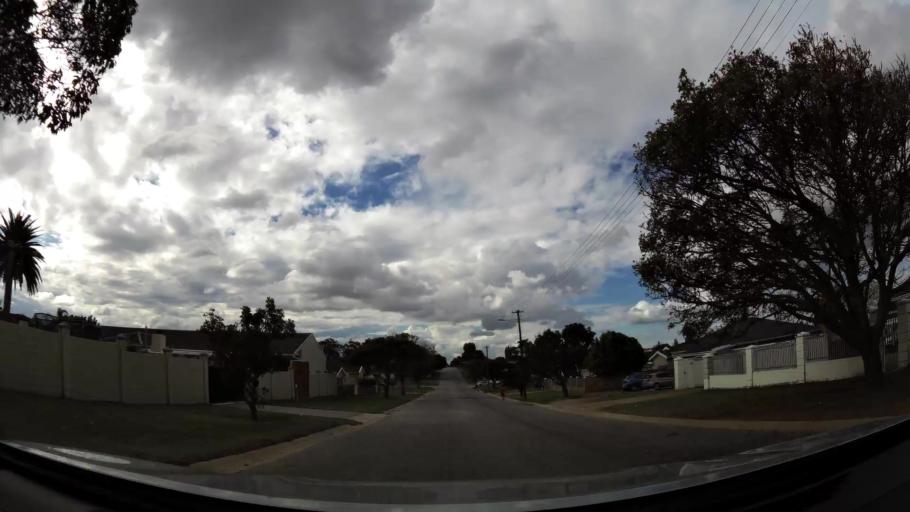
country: ZA
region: Eastern Cape
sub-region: Nelson Mandela Bay Metropolitan Municipality
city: Port Elizabeth
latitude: -33.9420
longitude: 25.5229
